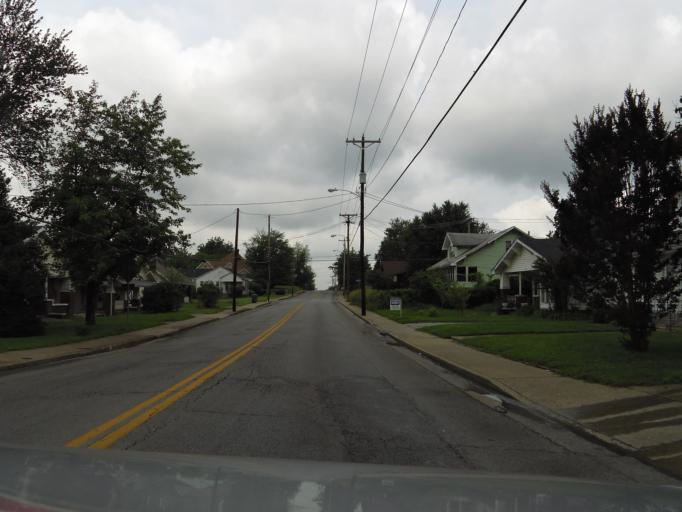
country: US
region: Kentucky
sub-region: Hopkins County
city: Madisonville
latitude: 37.3334
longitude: -87.5018
